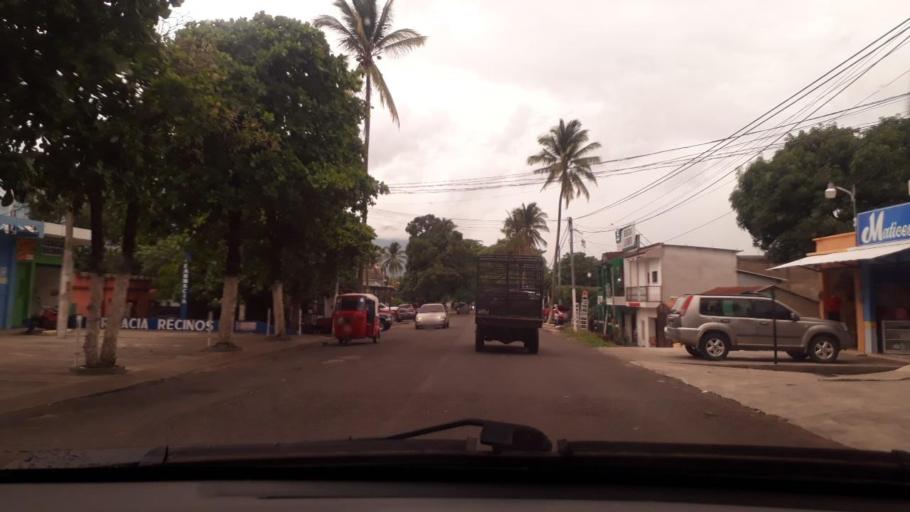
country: GT
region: Jutiapa
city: Jalpatagua
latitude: 14.1351
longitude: -90.0094
